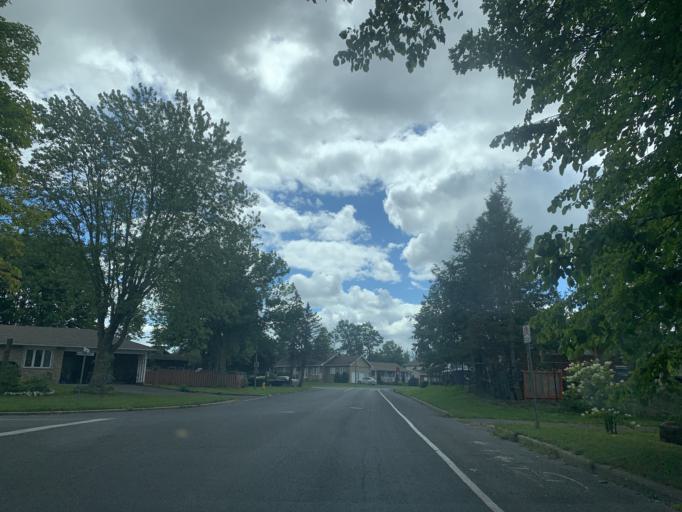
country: CA
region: Ontario
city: Hawkesbury
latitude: 45.6048
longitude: -74.6007
